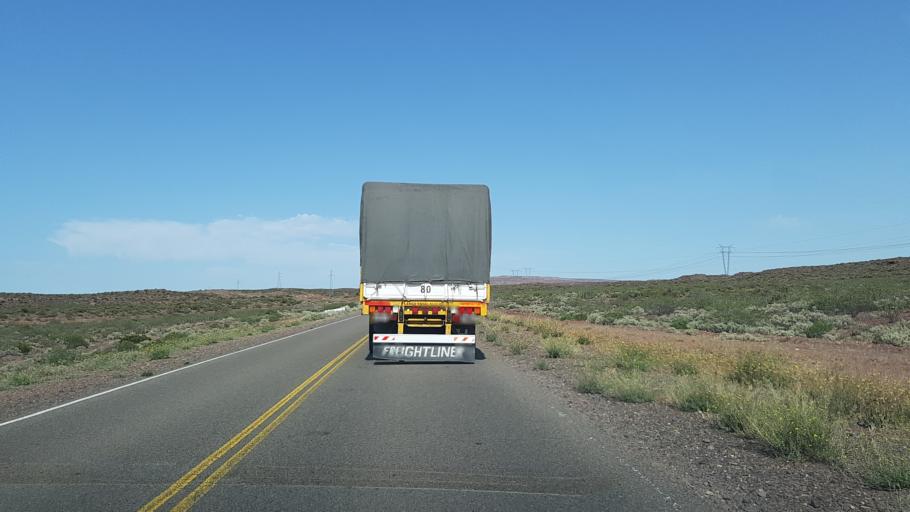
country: AR
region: Neuquen
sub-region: Departamento de Picun Leufu
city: Picun Leufu
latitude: -39.2994
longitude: -68.9120
